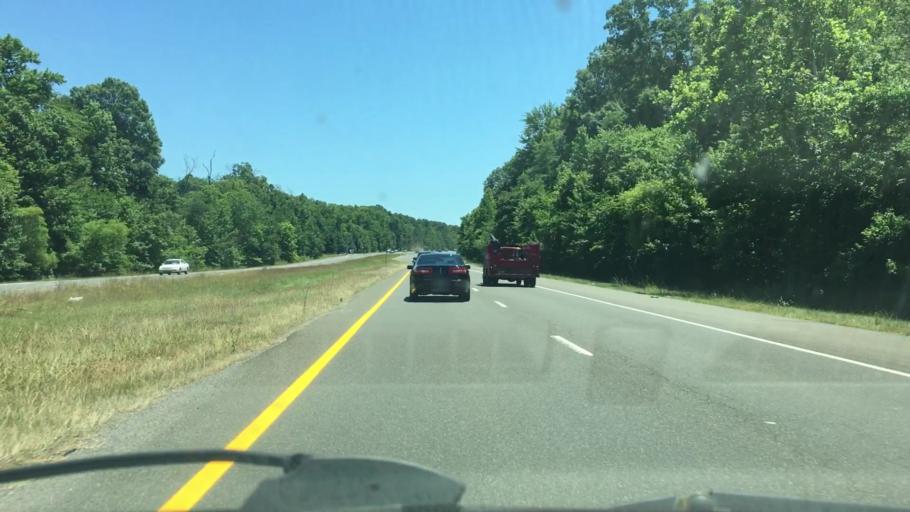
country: US
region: Maryland
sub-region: Prince George's County
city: Glenn Dale
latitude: 38.9847
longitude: -76.8121
